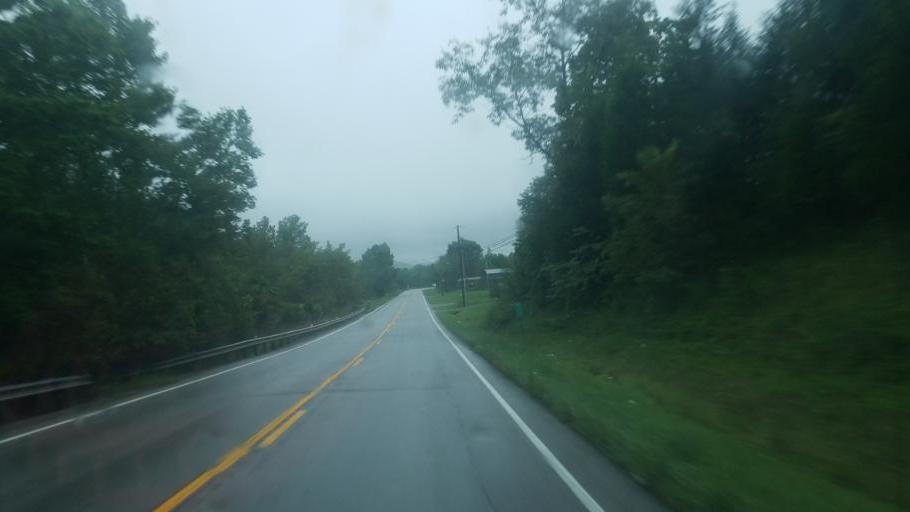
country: US
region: Kentucky
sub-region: Fleming County
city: Flemingsburg
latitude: 38.3767
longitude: -83.6360
